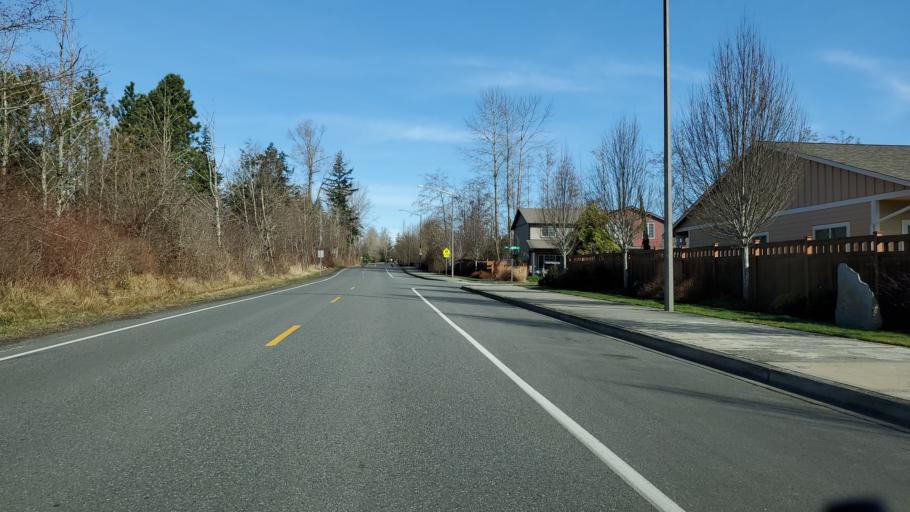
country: US
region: Washington
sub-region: Skagit County
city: Mount Vernon
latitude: 48.4398
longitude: -122.3026
